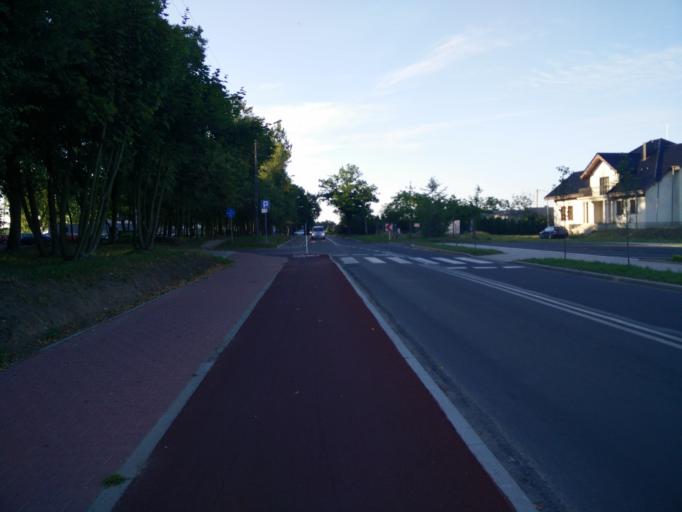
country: PL
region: Greater Poland Voivodeship
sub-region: Powiat sredzki
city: Sroda Wielkopolska
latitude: 52.2360
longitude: 17.2937
